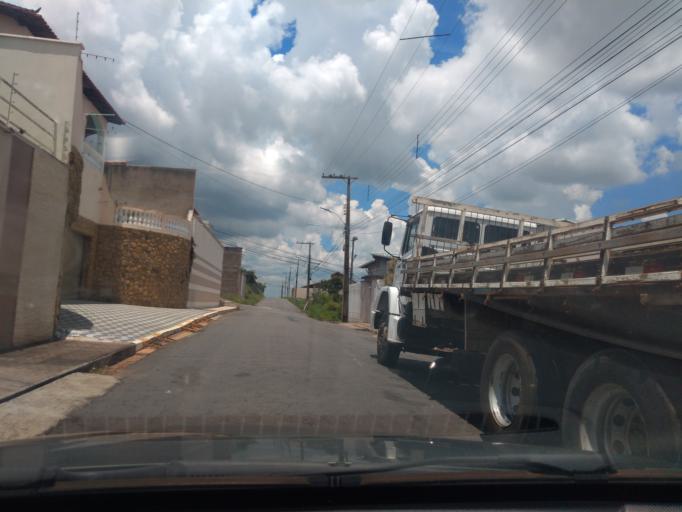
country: BR
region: Minas Gerais
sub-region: Tres Coracoes
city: Tres Coracoes
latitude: -21.6918
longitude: -45.2634
